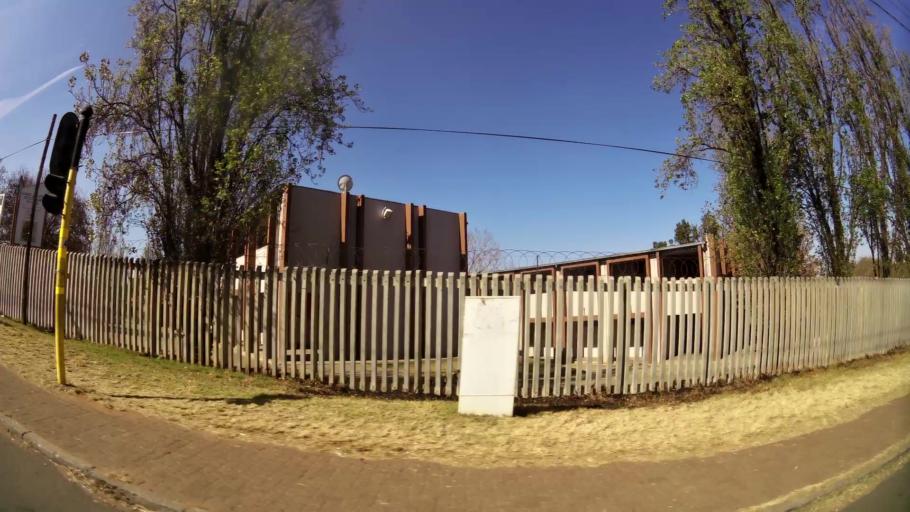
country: ZA
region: Gauteng
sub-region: City of Johannesburg Metropolitan Municipality
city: Johannesburg
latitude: -26.1892
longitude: 27.9596
